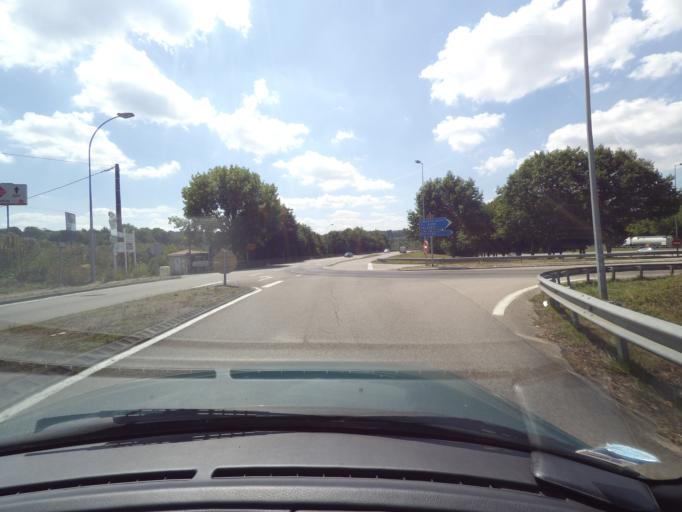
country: FR
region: Limousin
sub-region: Departement de la Haute-Vienne
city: Condat-sur-Vienne
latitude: 45.8085
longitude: 1.2992
